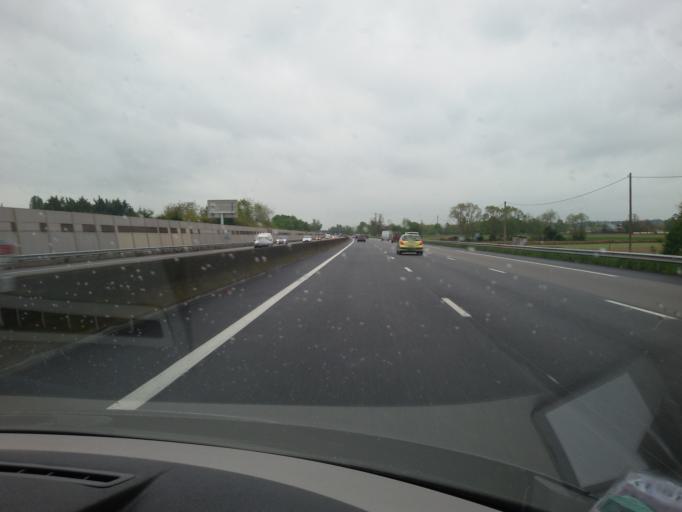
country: FR
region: Rhone-Alpes
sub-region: Departement du Rhone
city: Saint-Georges-de-Reneins
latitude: 46.0602
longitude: 4.7368
